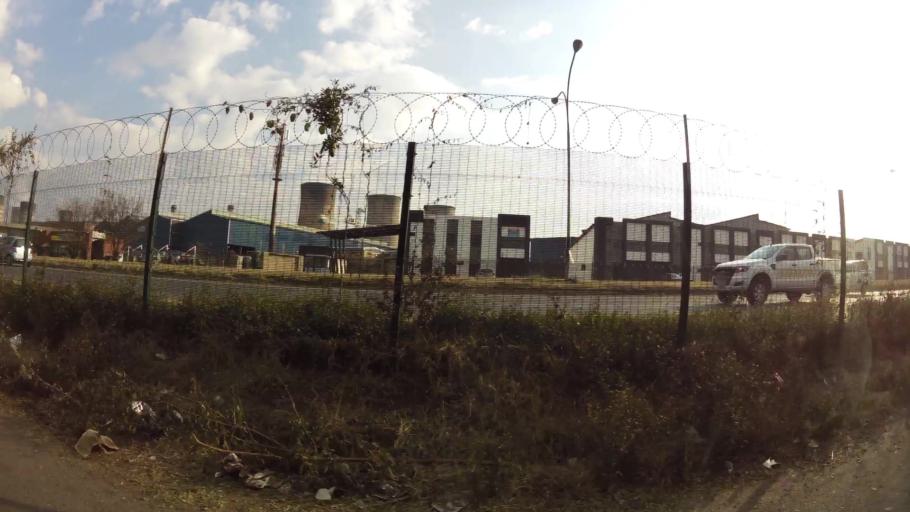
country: ZA
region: Gauteng
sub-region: City of Johannesburg Metropolitan Municipality
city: Modderfontein
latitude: -26.1109
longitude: 28.1977
